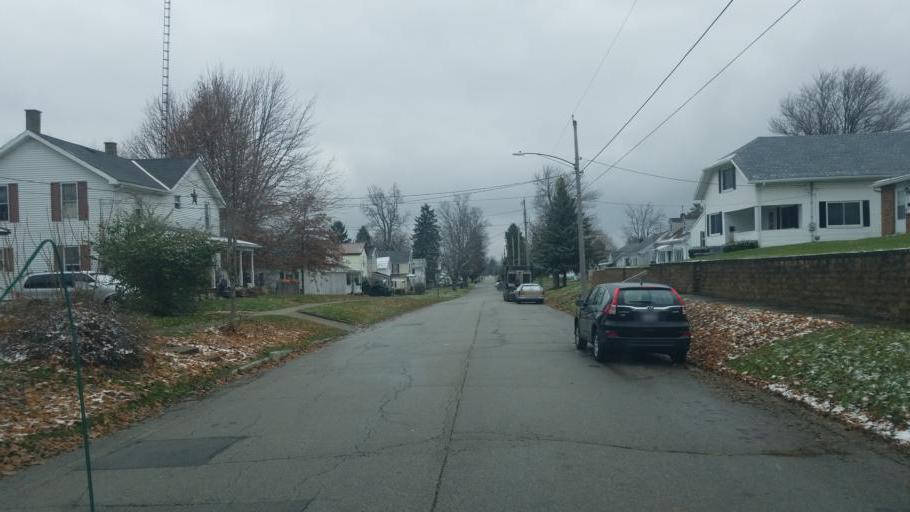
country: US
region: Ohio
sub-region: Richland County
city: Shelby
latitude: 40.8894
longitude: -82.6548
